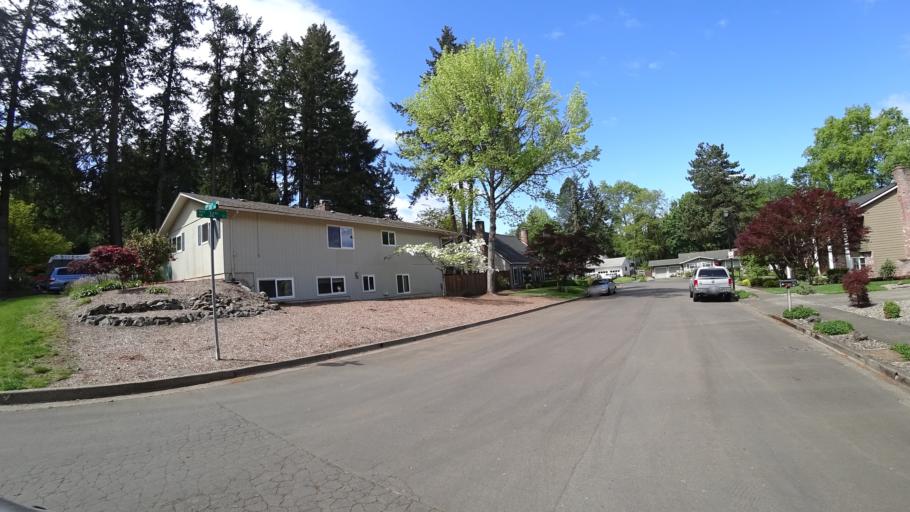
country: US
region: Oregon
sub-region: Washington County
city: Beaverton
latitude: 45.4647
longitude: -122.8173
